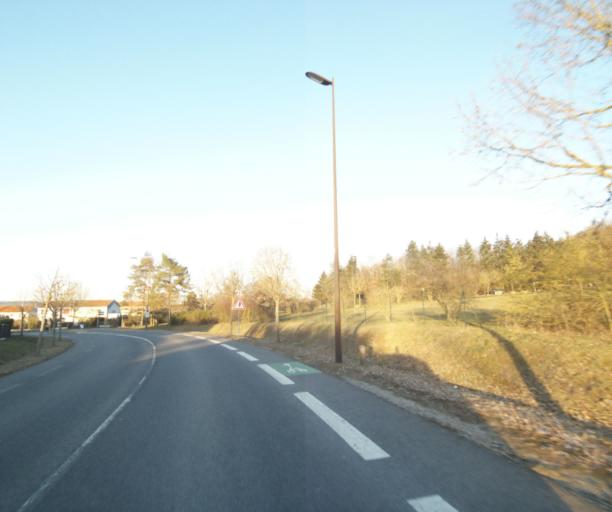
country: FR
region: Lorraine
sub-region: Departement de Meurthe-et-Moselle
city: Pulnoy
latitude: 48.6947
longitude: 6.2553
